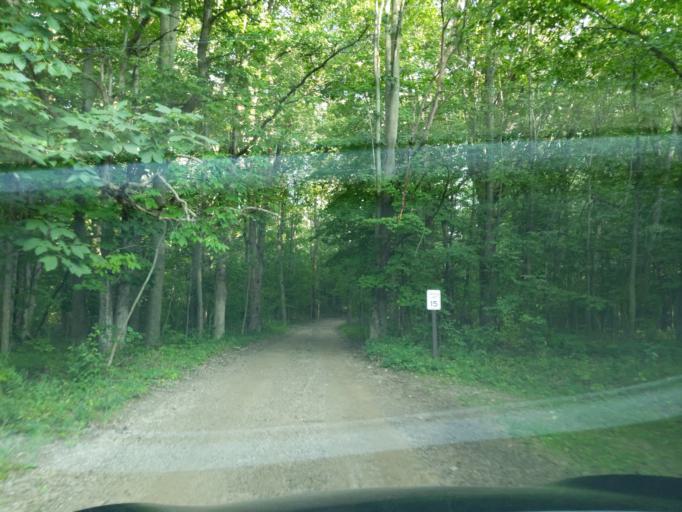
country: US
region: Michigan
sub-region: Eaton County
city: Dimondale
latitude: 42.6004
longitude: -84.5938
